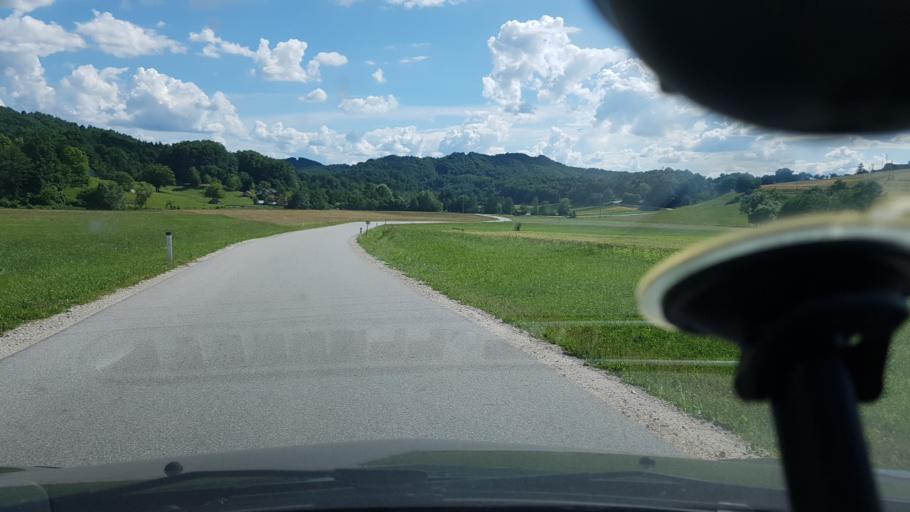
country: SI
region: Rogatec
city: Rogatec
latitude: 46.2511
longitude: 15.7310
